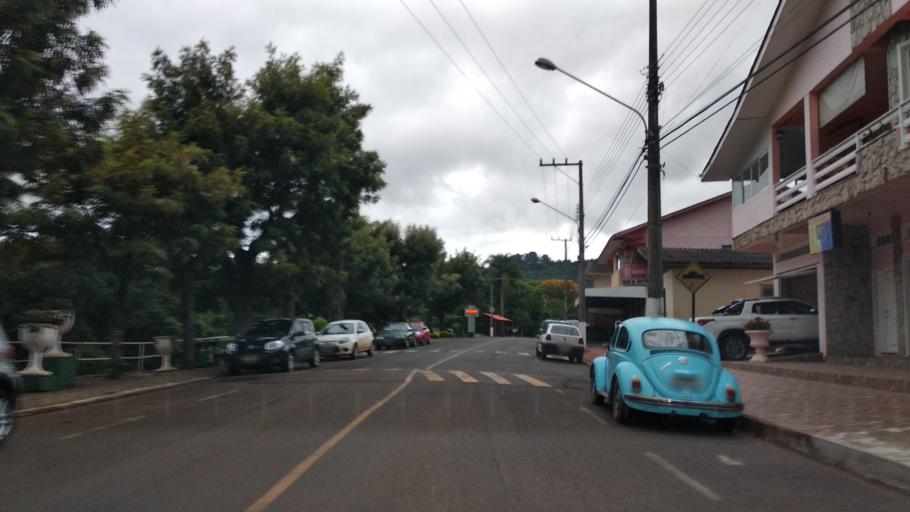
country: BR
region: Santa Catarina
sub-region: Videira
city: Videira
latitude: -27.0461
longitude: -51.2286
